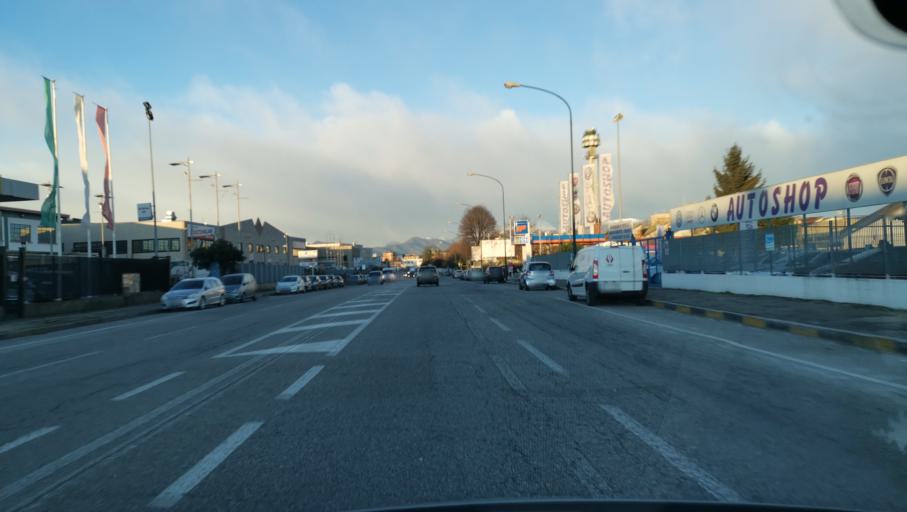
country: IT
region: Piedmont
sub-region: Provincia di Torino
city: Turin
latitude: 45.1107
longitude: 7.6754
